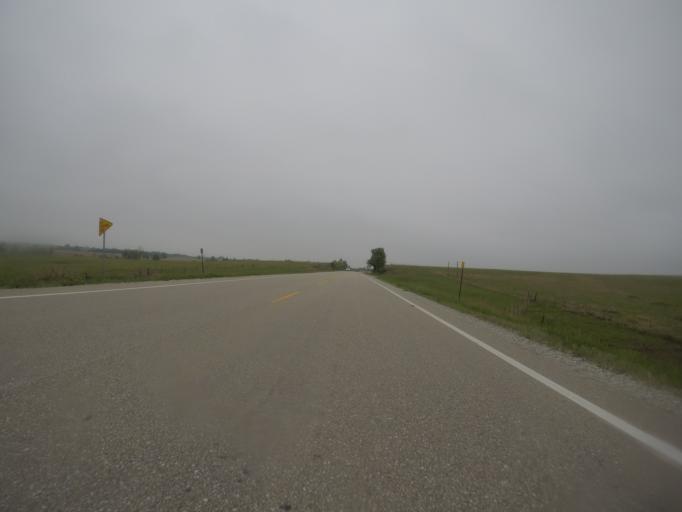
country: US
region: Kansas
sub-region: Pottawatomie County
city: Westmoreland
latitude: 39.4881
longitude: -96.4171
